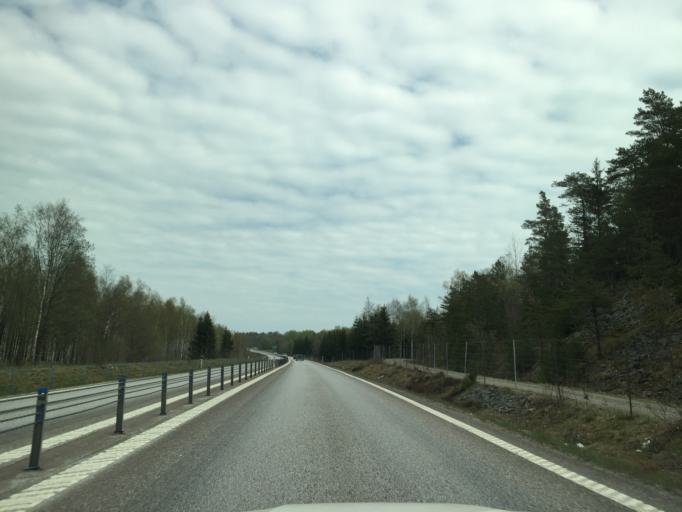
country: SE
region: Vaestra Goetaland
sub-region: Uddevalla Kommun
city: Uddevalla
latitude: 58.3264
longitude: 11.9662
